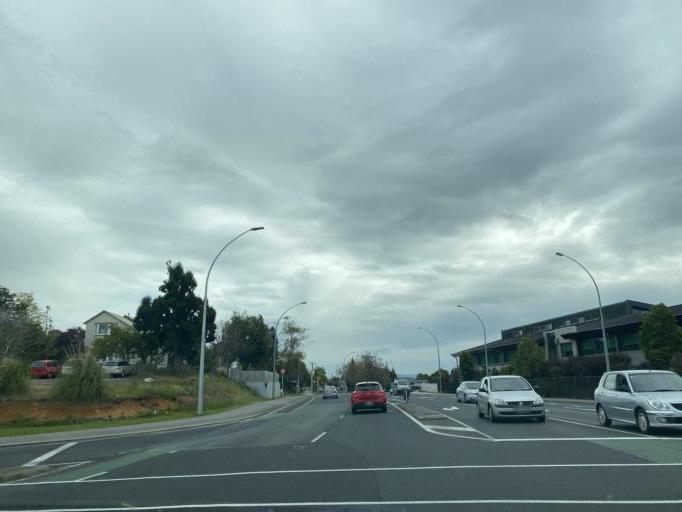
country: NZ
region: Waikato
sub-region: Hamilton City
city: Hamilton
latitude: -37.8082
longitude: 175.2803
